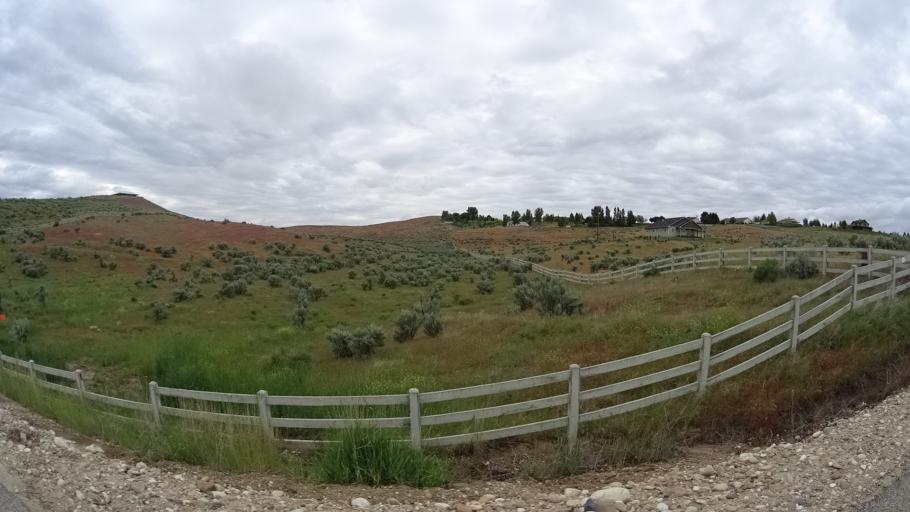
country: US
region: Idaho
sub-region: Ada County
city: Eagle
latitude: 43.7353
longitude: -116.3935
